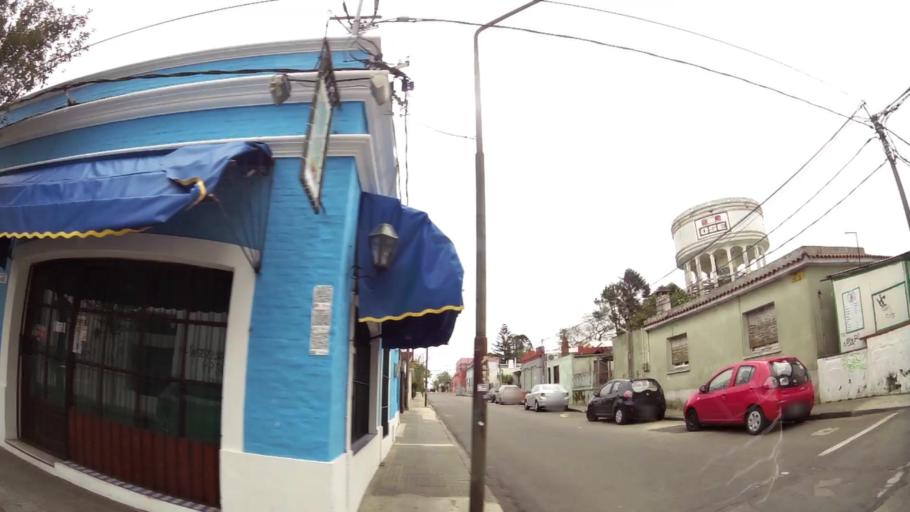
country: UY
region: Maldonado
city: Maldonado
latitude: -34.9118
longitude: -54.9576
